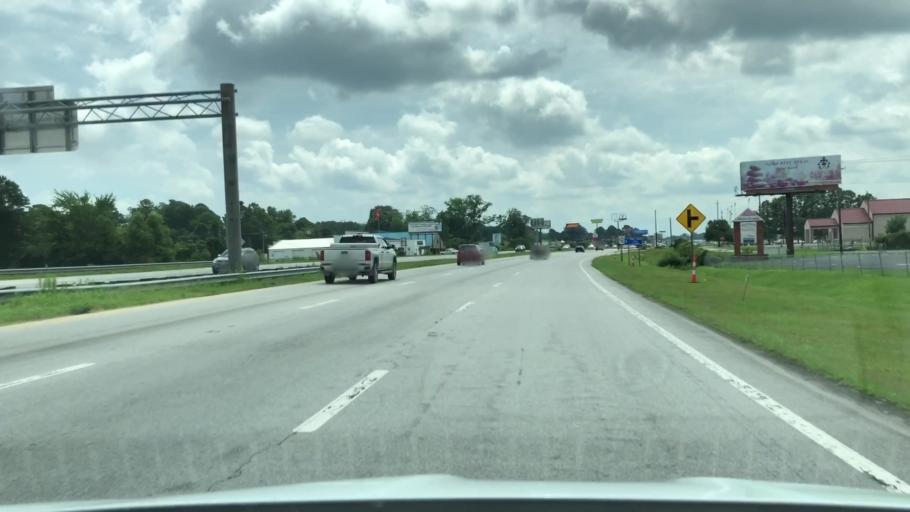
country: US
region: North Carolina
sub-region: Craven County
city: James City
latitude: 35.0865
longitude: -77.0333
